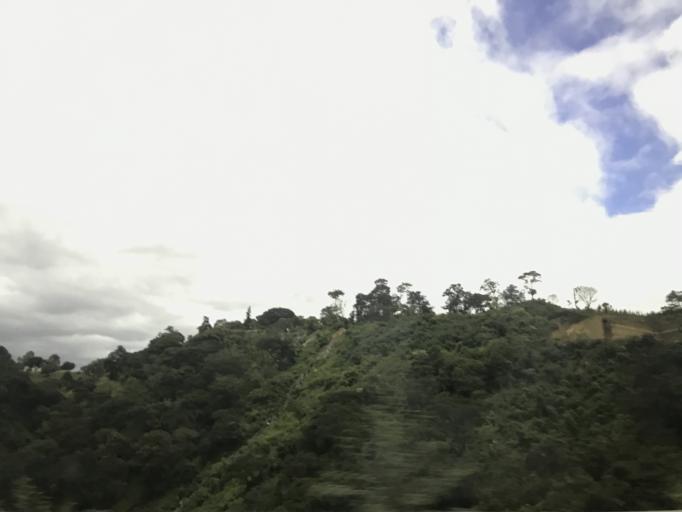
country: GT
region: Chimaltenango
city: Parramos
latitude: 14.6245
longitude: -90.8019
